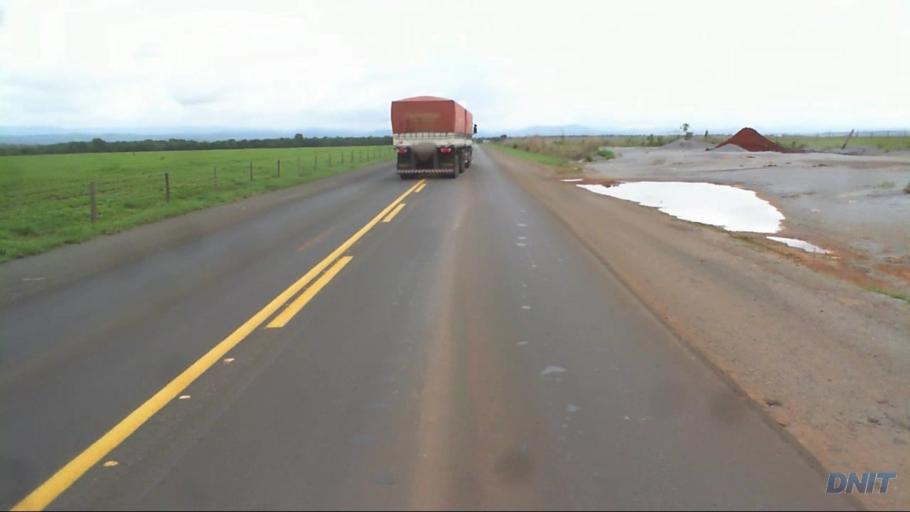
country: BR
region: Goias
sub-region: Padre Bernardo
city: Padre Bernardo
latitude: -15.1713
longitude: -48.3673
